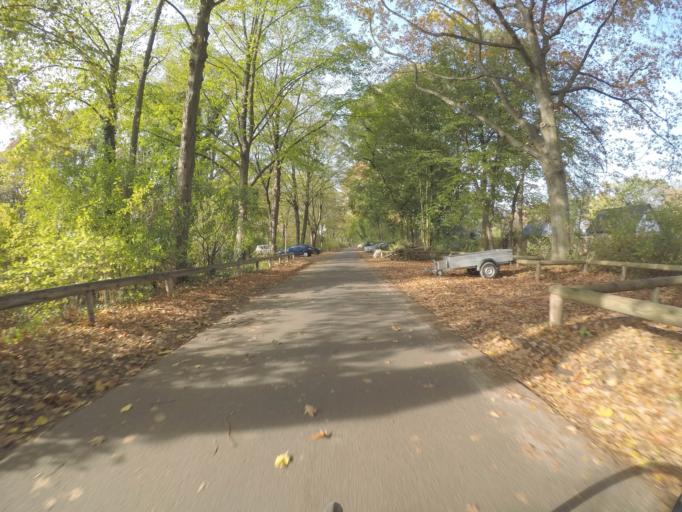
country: DE
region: Berlin
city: Britz
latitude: 52.4254
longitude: 13.4192
